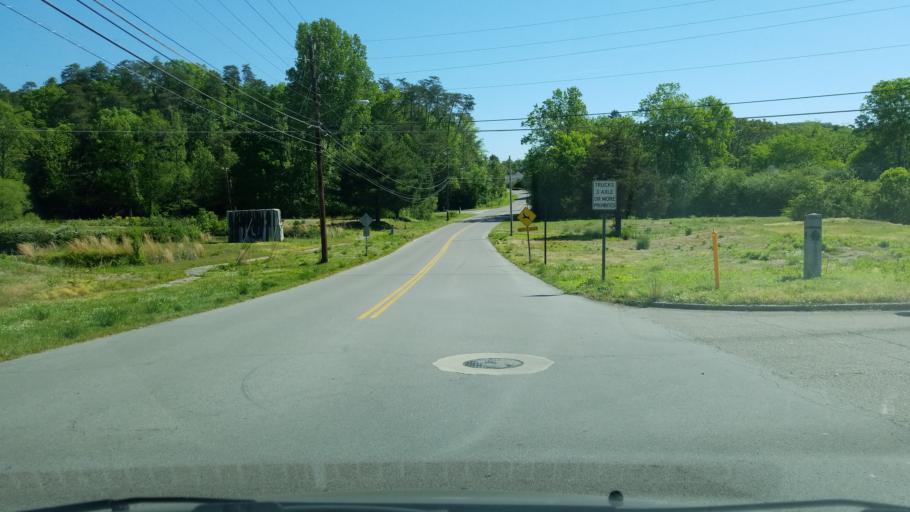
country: US
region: Tennessee
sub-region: Hamilton County
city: Red Bank
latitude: 35.1337
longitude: -85.3063
